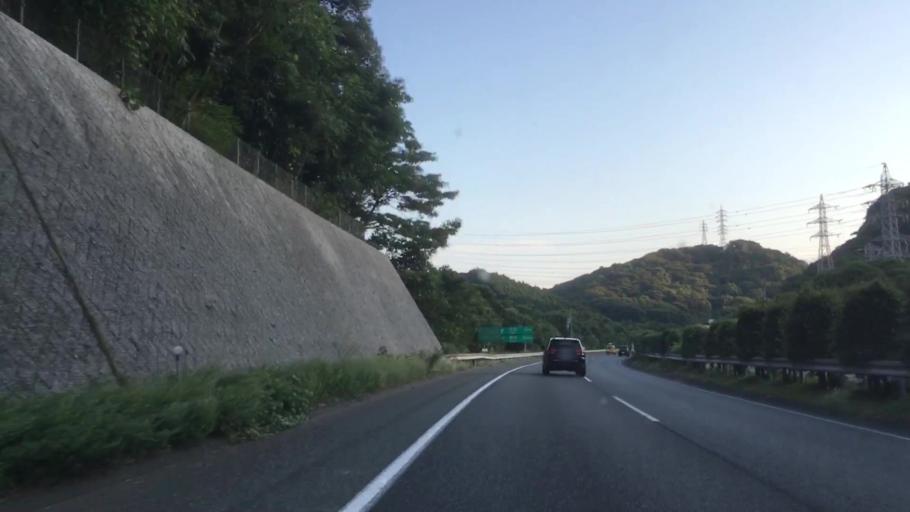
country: JP
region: Yamaguchi
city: Shimonoseki
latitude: 33.8970
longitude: 130.9724
